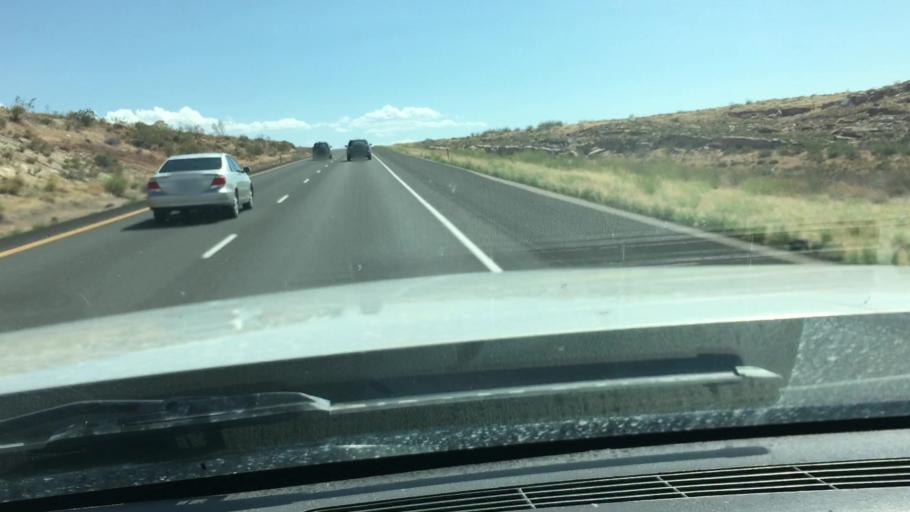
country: US
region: Utah
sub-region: Washington County
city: Washington
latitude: 37.1883
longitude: -113.4106
